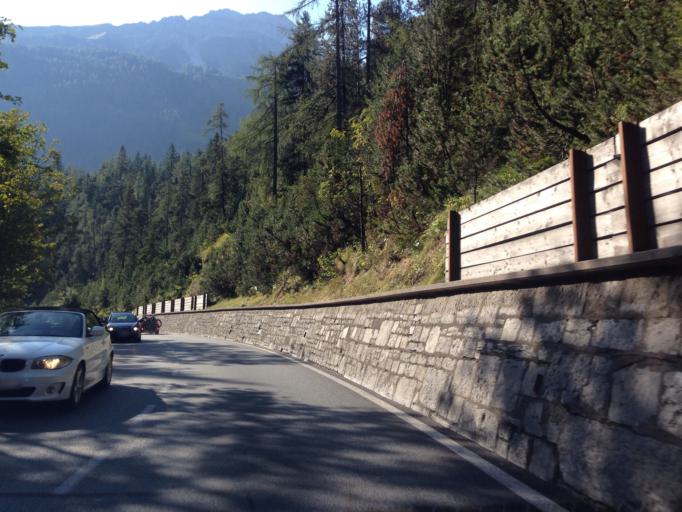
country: AT
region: Tyrol
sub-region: Politischer Bezirk Imst
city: Nassereith
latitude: 47.3599
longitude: 10.8453
